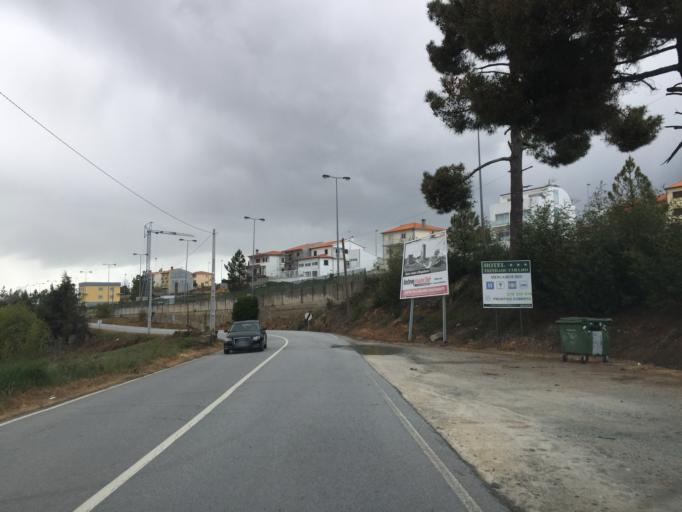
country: PT
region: Braganca
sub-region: Mogadouro
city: Mogadouro
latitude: 41.3418
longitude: -6.6989
